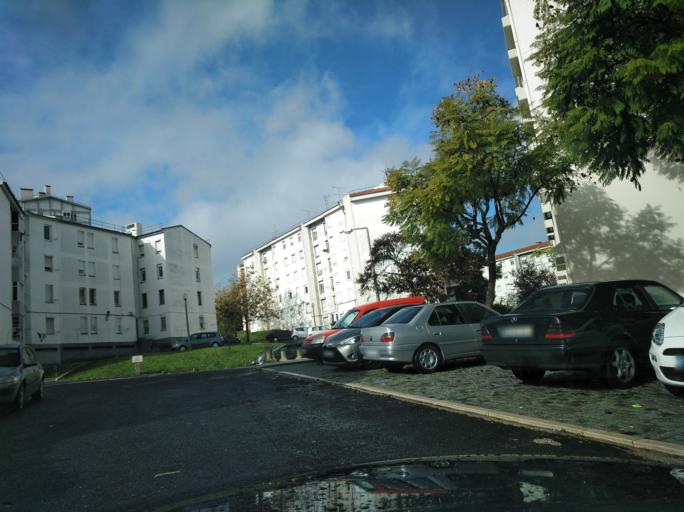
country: PT
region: Lisbon
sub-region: Loures
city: Moscavide
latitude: 38.7593
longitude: -9.1053
